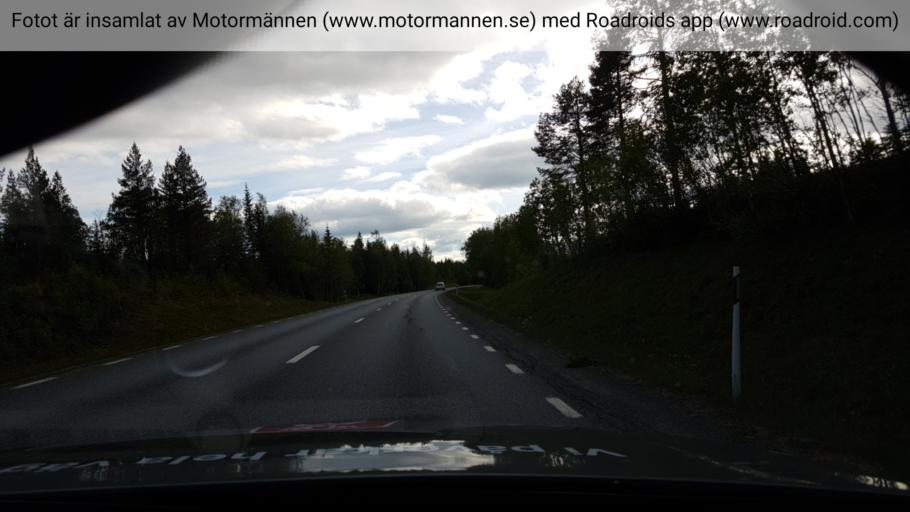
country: SE
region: Jaemtland
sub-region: OEstersunds Kommun
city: Lit
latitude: 63.4193
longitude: 15.1057
